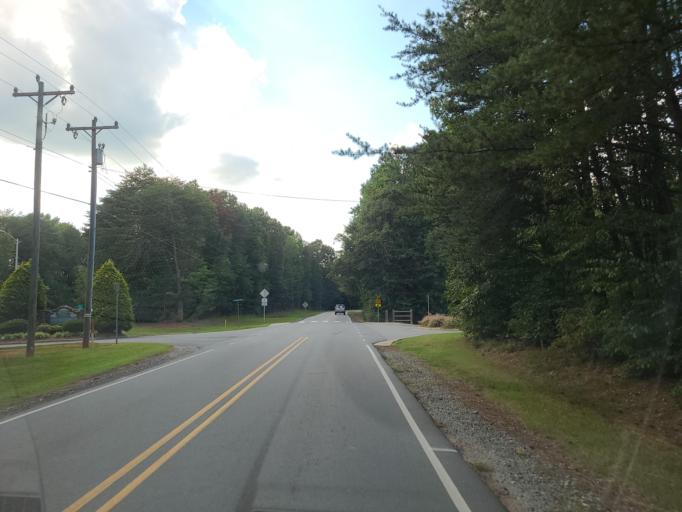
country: US
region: North Carolina
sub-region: Gaston County
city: Lowell
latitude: 35.2860
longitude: -81.1075
